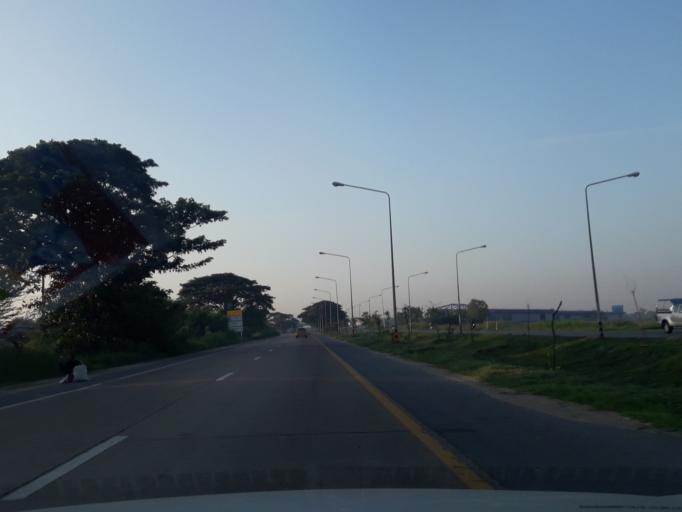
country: TH
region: Phra Nakhon Si Ayutthaya
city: Bang Ban
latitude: 14.3605
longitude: 100.5287
